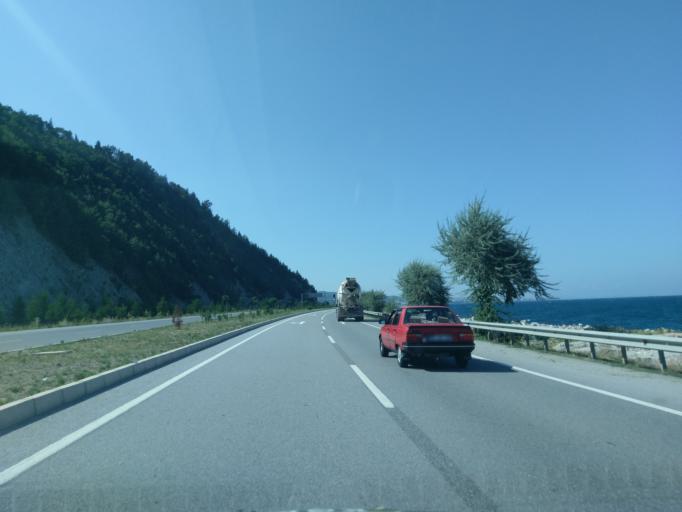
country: TR
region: Sinop
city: Gerze
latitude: 41.7473
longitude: 35.2437
